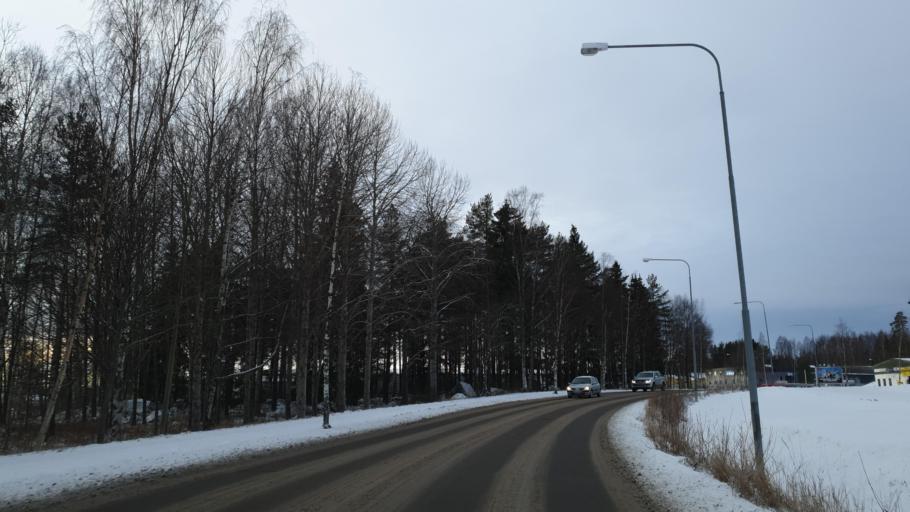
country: SE
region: Gaevleborg
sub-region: Soderhamns Kommun
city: Soderhamn
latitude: 61.3042
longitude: 17.0431
